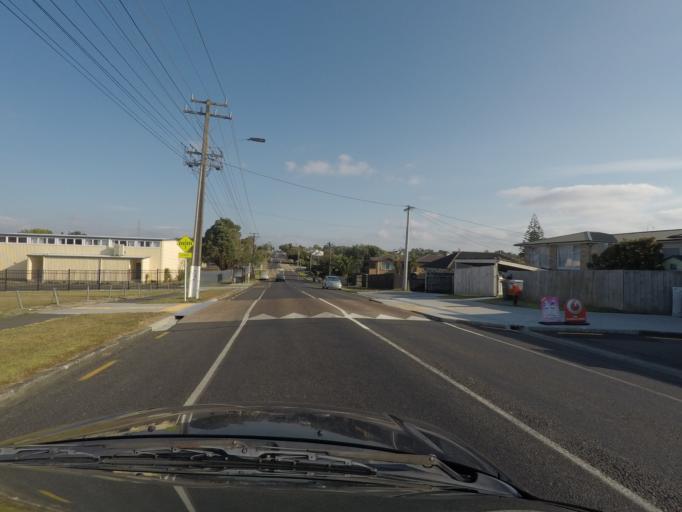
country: NZ
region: Auckland
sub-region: Auckland
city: Rosebank
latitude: -36.8598
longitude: 174.6442
